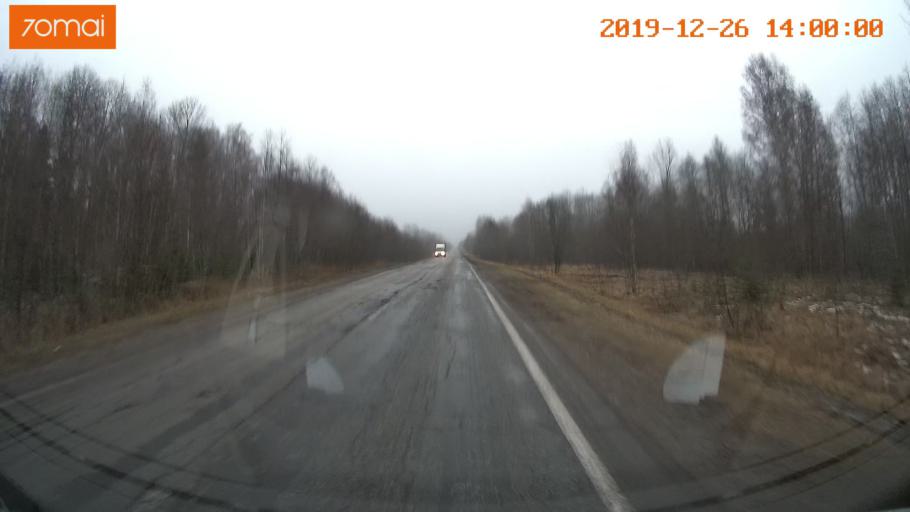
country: RU
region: Jaroslavl
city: Poshekhon'ye
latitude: 58.5612
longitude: 38.7353
